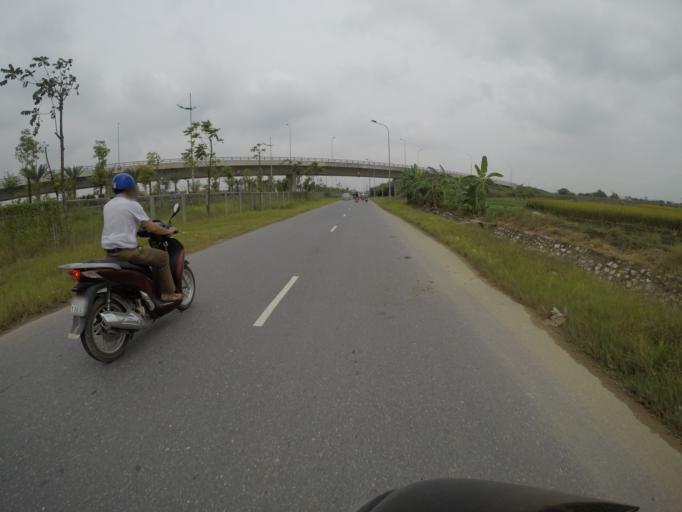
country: VN
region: Ha Noi
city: Dong Anh
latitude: 21.1742
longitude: 105.8245
